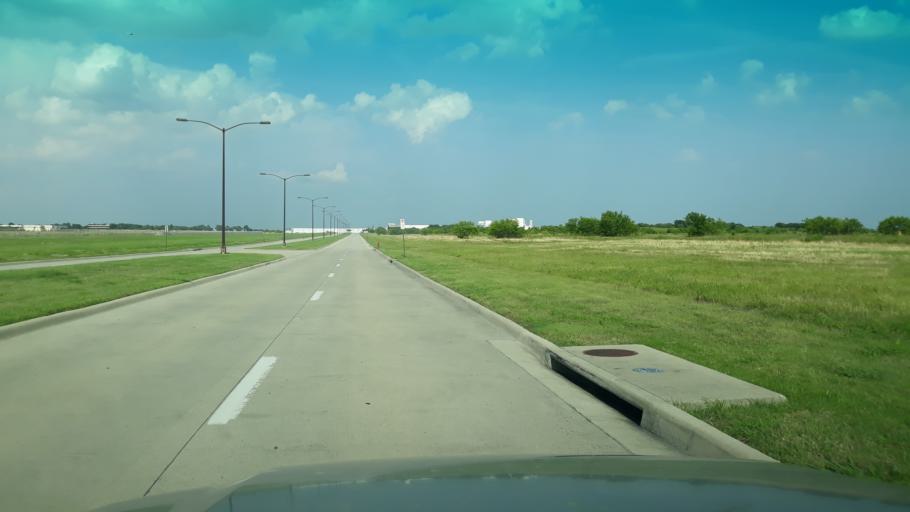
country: US
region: Texas
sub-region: Tarrant County
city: Euless
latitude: 32.8703
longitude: -97.0318
